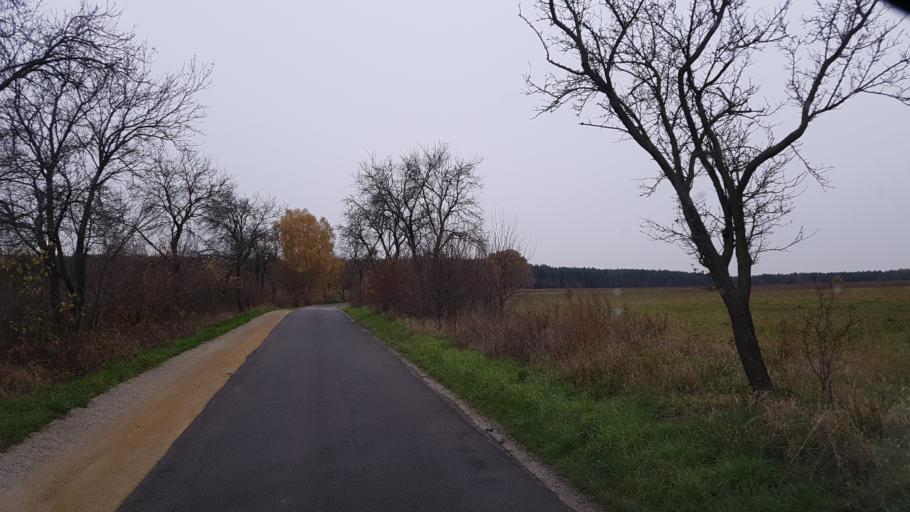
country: DE
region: Brandenburg
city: Crinitz
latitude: 51.7329
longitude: 13.7627
